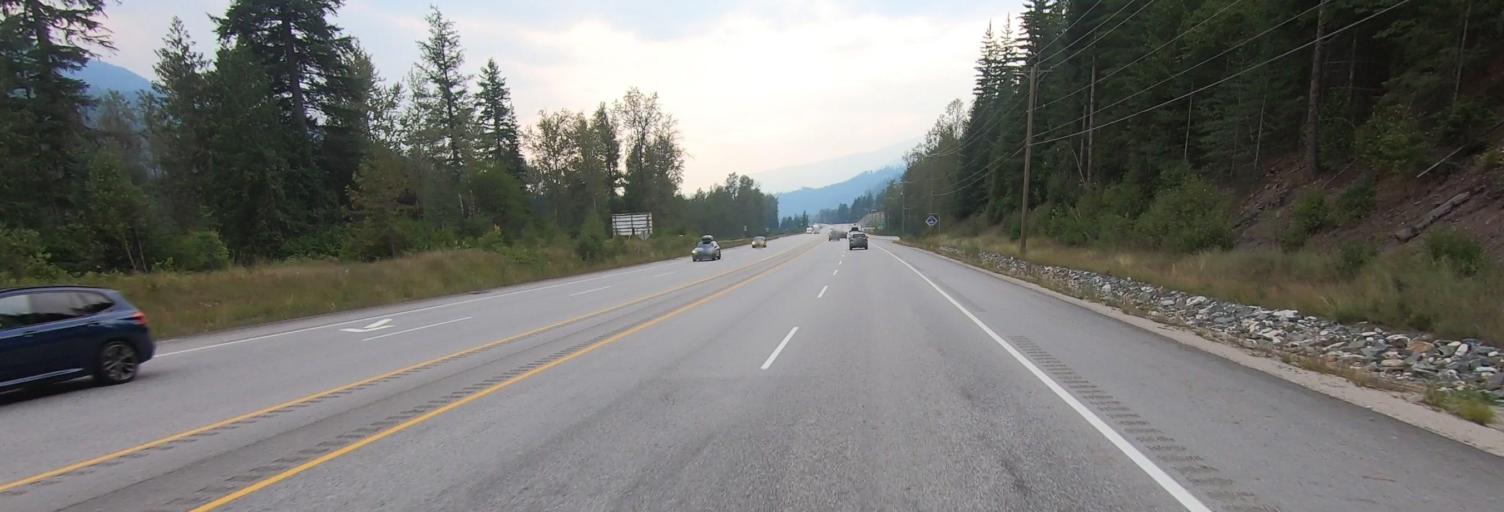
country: CA
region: British Columbia
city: Sicamous
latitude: 51.0021
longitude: -118.6786
